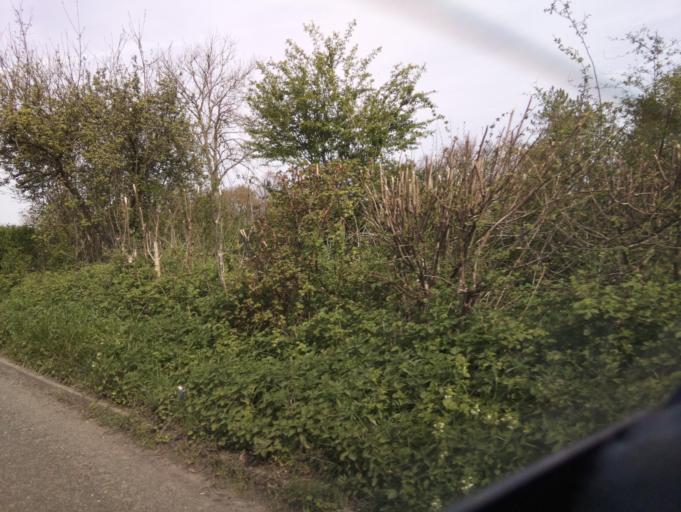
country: GB
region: England
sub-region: Somerset
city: Street
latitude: 51.1112
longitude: -2.7609
